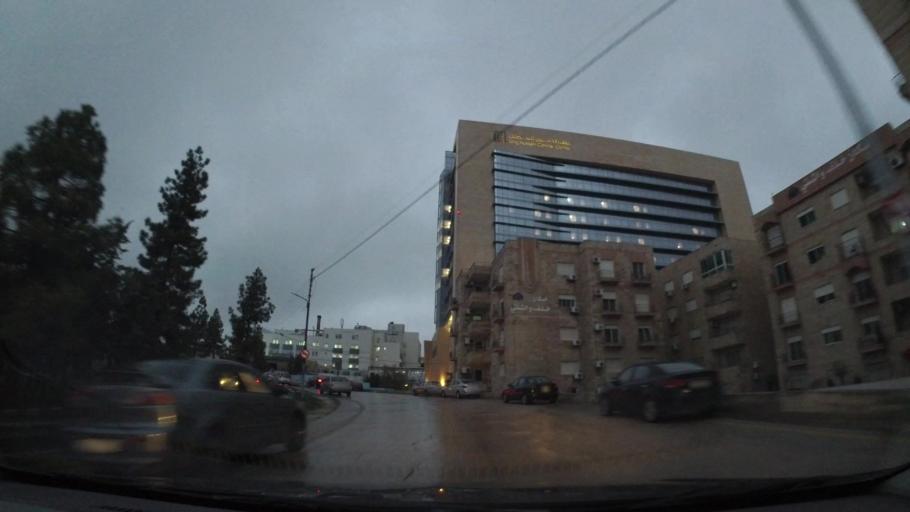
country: JO
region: Amman
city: Al Jubayhah
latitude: 32.0031
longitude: 35.8763
